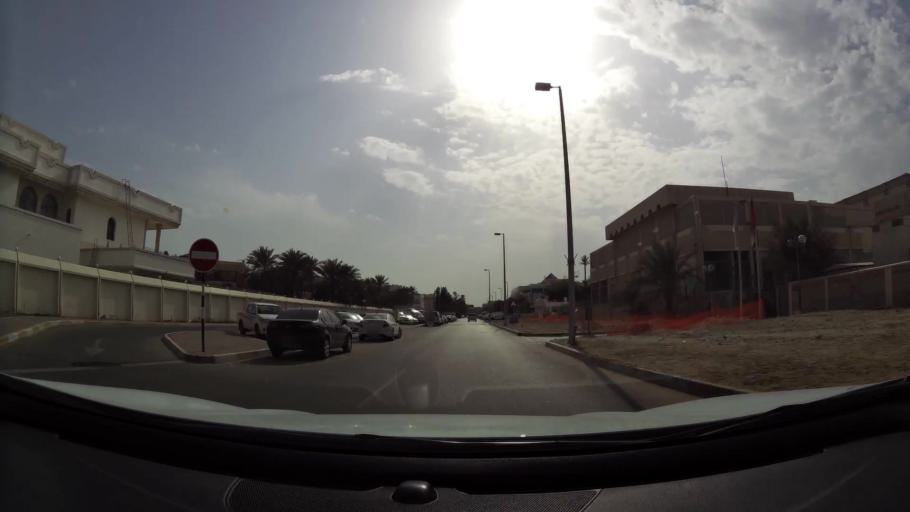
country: AE
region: Abu Dhabi
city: Abu Dhabi
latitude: 24.4690
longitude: 54.3536
